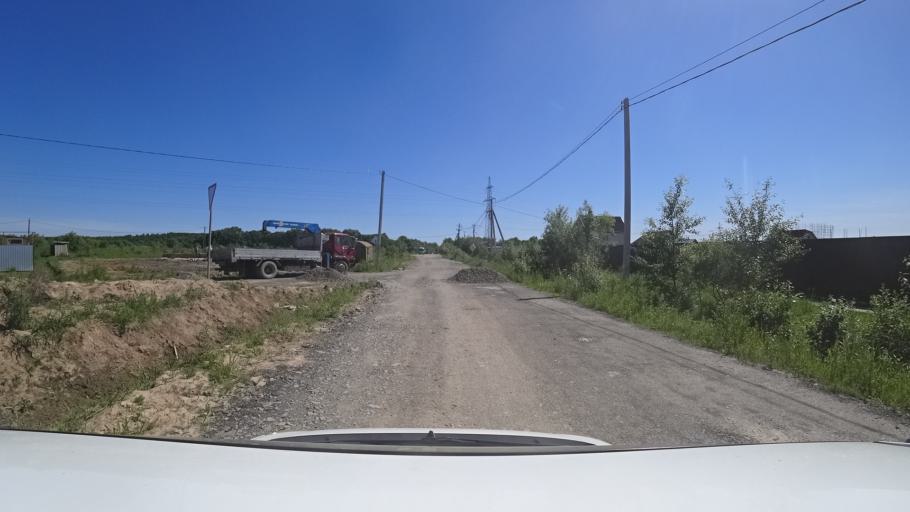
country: RU
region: Khabarovsk Krai
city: Topolevo
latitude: 48.5633
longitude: 135.1927
